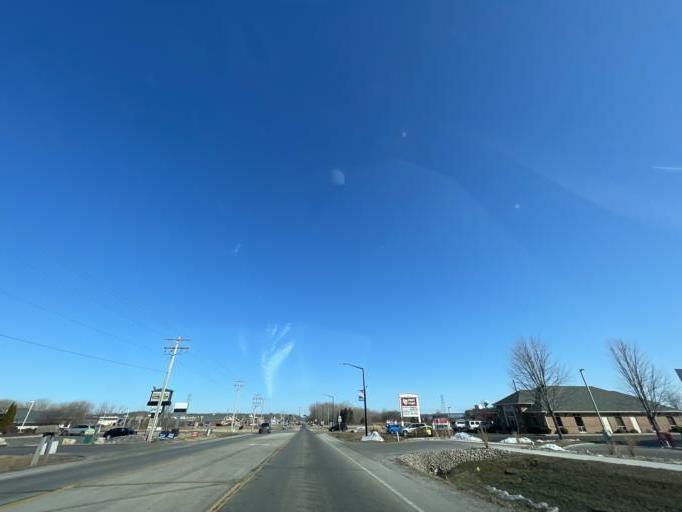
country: US
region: Wisconsin
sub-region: Brown County
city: Howard
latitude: 44.5909
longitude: -88.0806
